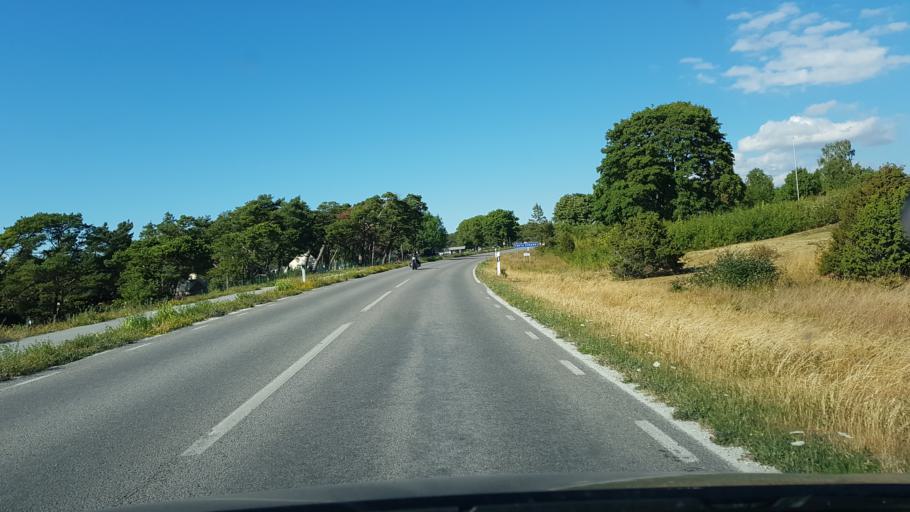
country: SE
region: Gotland
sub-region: Gotland
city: Klintehamn
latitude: 57.4817
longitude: 18.1271
